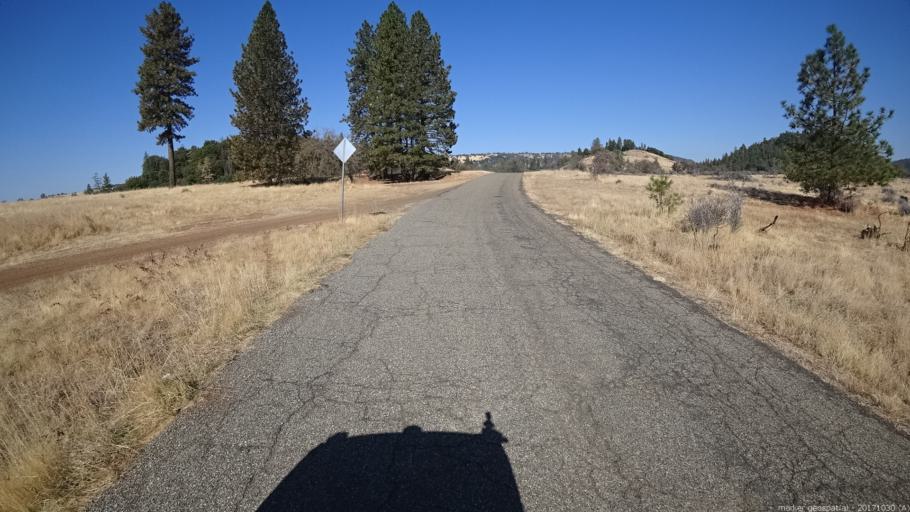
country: US
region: California
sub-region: Shasta County
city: Shingletown
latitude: 40.5354
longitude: -121.9335
